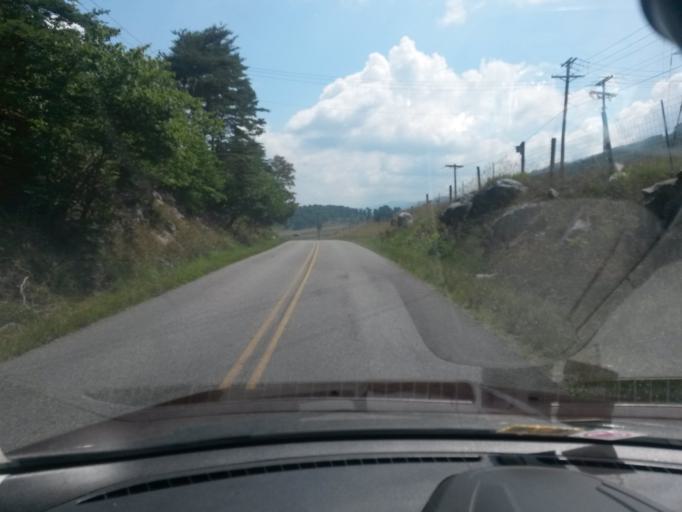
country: US
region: Virginia
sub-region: Giles County
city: Narrows
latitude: 37.3723
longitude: -80.7987
